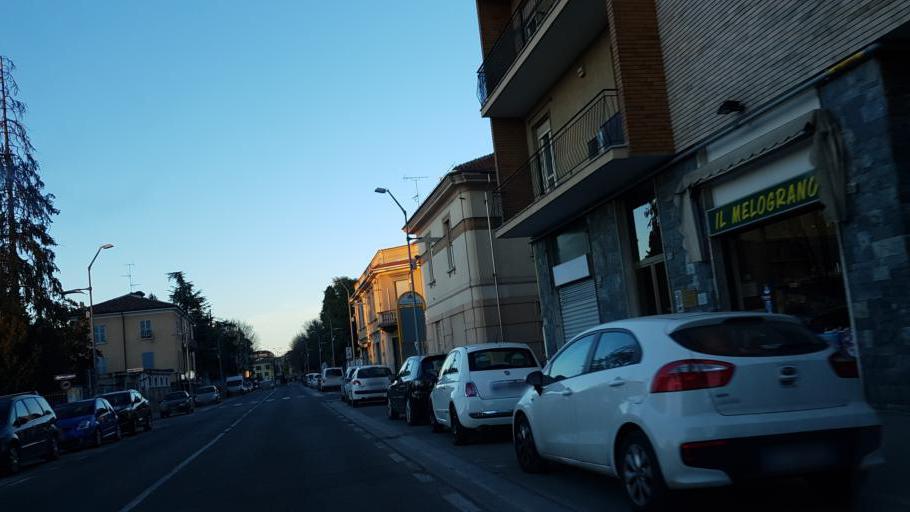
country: IT
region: Piedmont
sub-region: Provincia di Alessandria
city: Tortona
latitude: 44.8910
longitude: 8.8607
